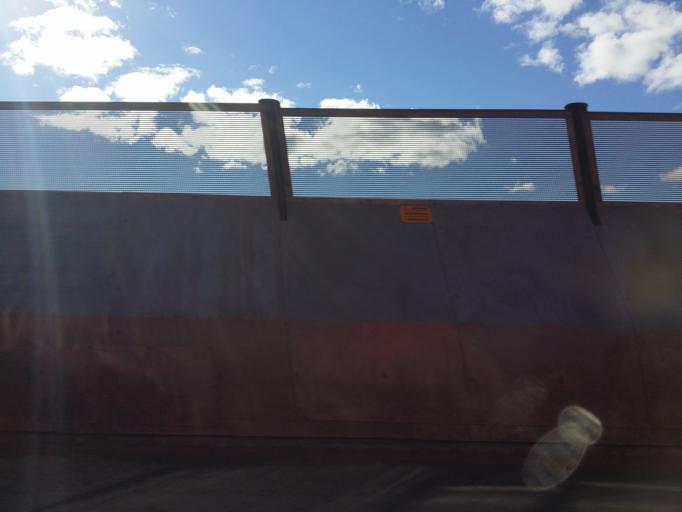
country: NO
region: Oslo
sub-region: Oslo
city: Oslo
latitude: 59.8963
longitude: 10.7561
